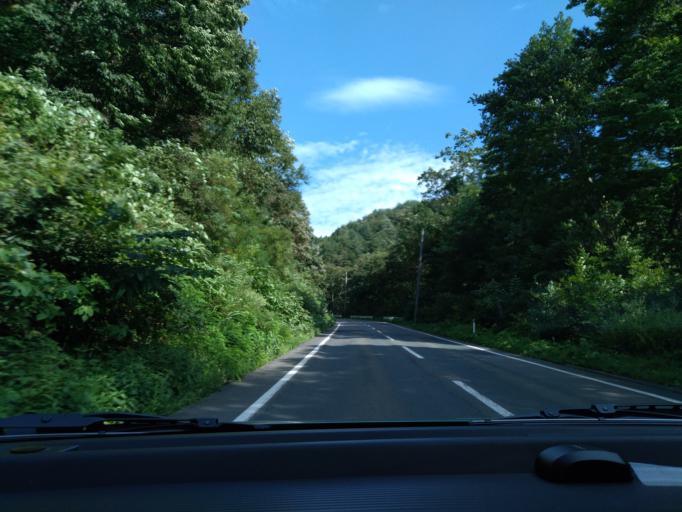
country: JP
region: Iwate
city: Shizukuishi
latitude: 39.6370
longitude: 141.0262
